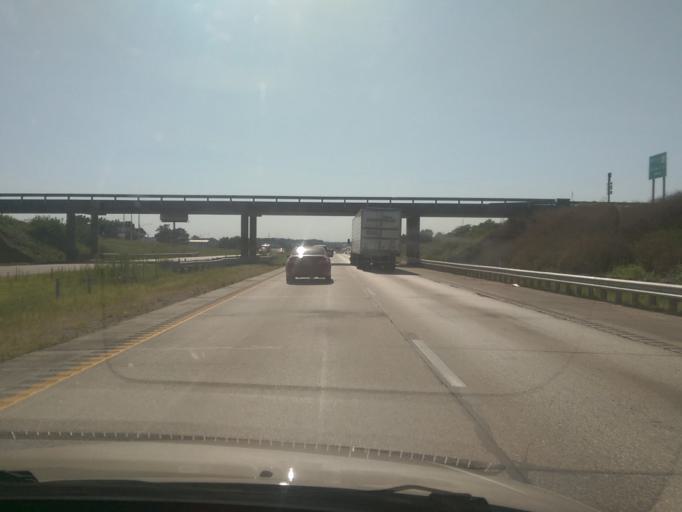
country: US
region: Missouri
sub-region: Saline County
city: Sweet Springs
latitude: 38.9771
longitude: -93.4142
